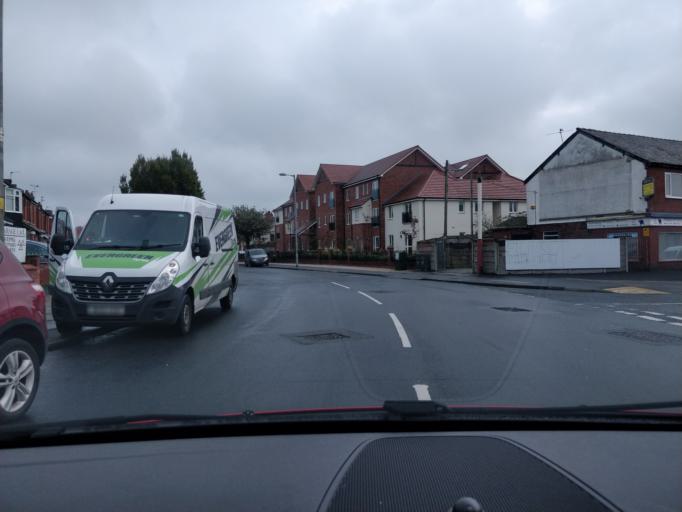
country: GB
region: England
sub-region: Sefton
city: Southport
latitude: 53.6033
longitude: -3.0314
